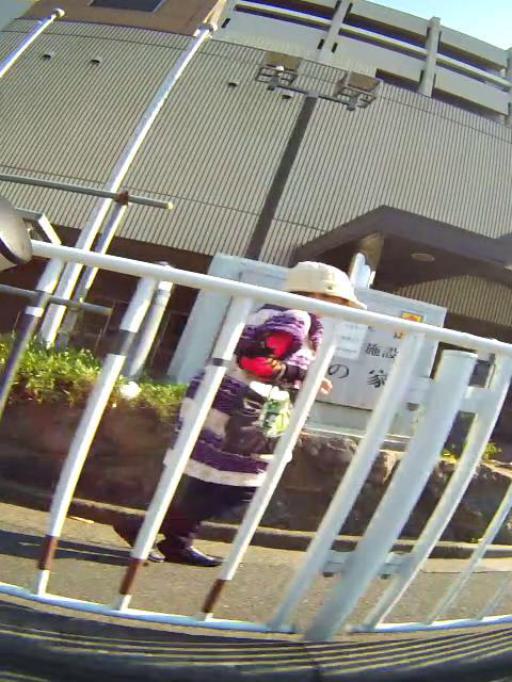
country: JP
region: Osaka
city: Yao
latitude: 34.6583
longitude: 135.6398
